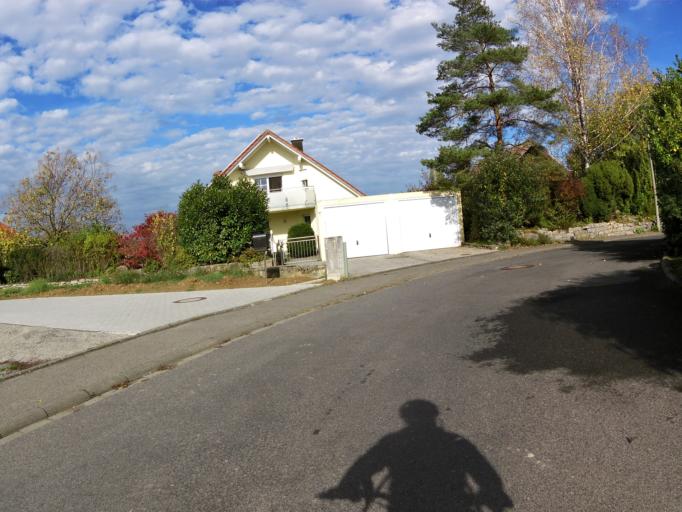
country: DE
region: Bavaria
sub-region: Regierungsbezirk Unterfranken
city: Frickenhausen
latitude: 49.7070
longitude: 10.0767
